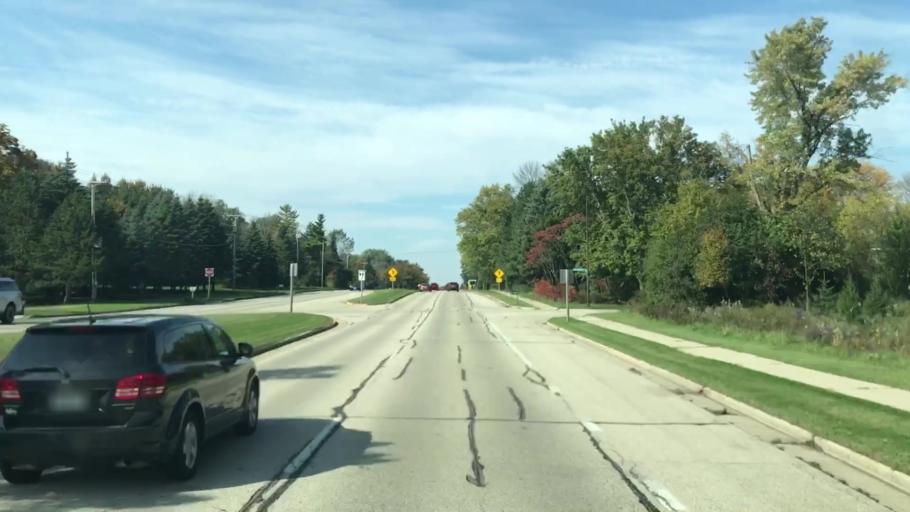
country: US
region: Wisconsin
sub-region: Ozaukee County
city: Thiensville
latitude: 43.2216
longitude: -87.9500
